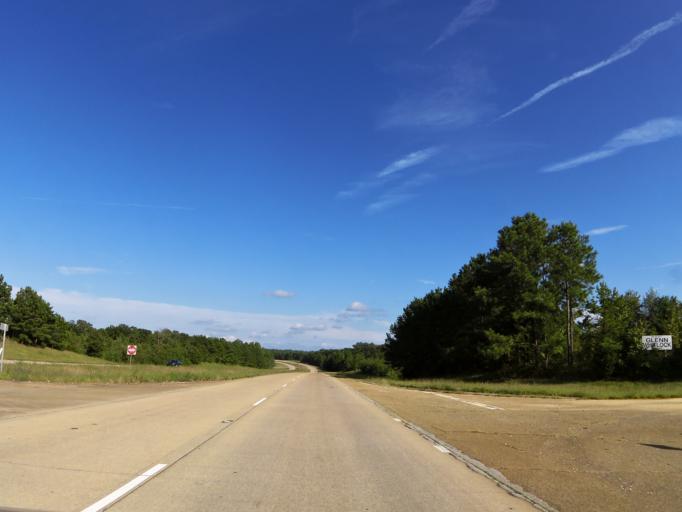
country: US
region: Mississippi
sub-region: Tishomingo County
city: Iuka
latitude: 34.7851
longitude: -88.1852
